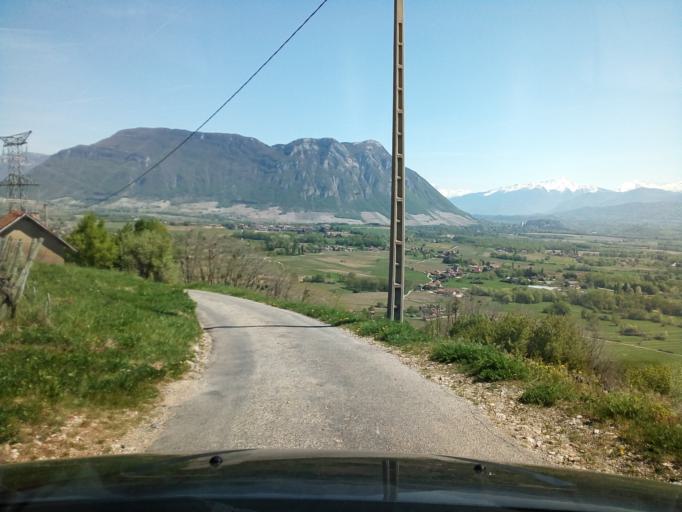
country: FR
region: Rhone-Alpes
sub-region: Departement de l'Isere
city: Chapareillan
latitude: 45.4820
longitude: 5.9772
